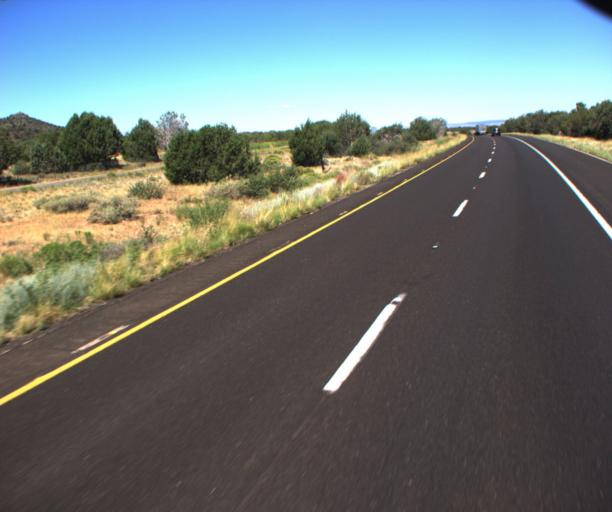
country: US
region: Arizona
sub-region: Yavapai County
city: Paulden
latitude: 35.2693
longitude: -112.7286
